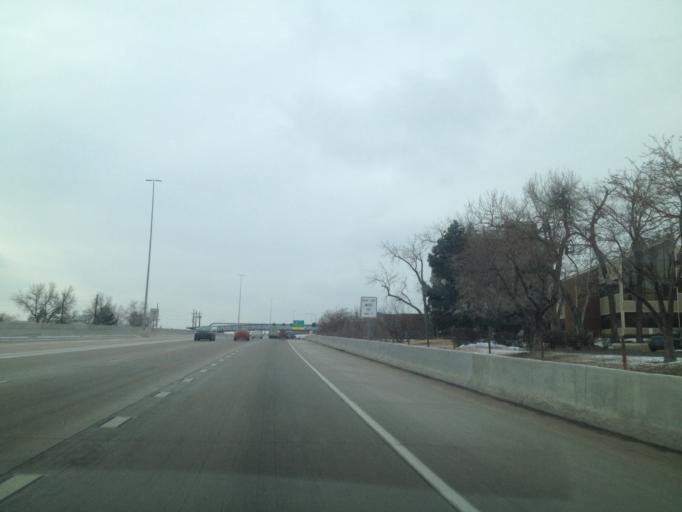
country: US
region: Colorado
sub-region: Adams County
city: Westminster
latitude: 39.8538
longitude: -105.0509
